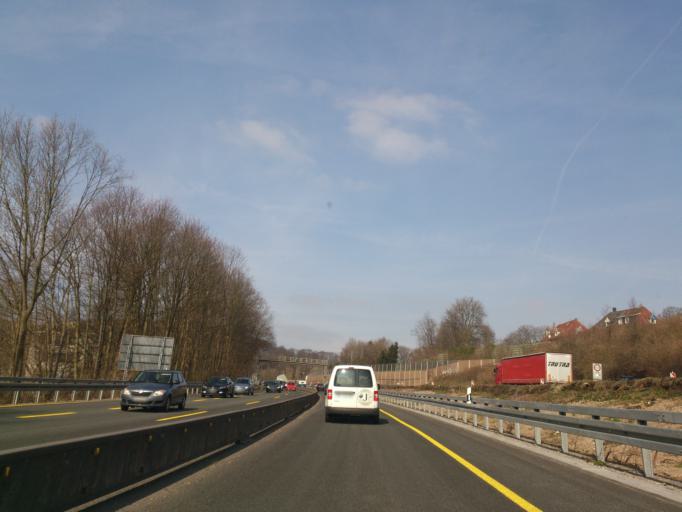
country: DE
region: North Rhine-Westphalia
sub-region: Regierungsbezirk Dusseldorf
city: Wuppertal
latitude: 51.2573
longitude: 7.1114
